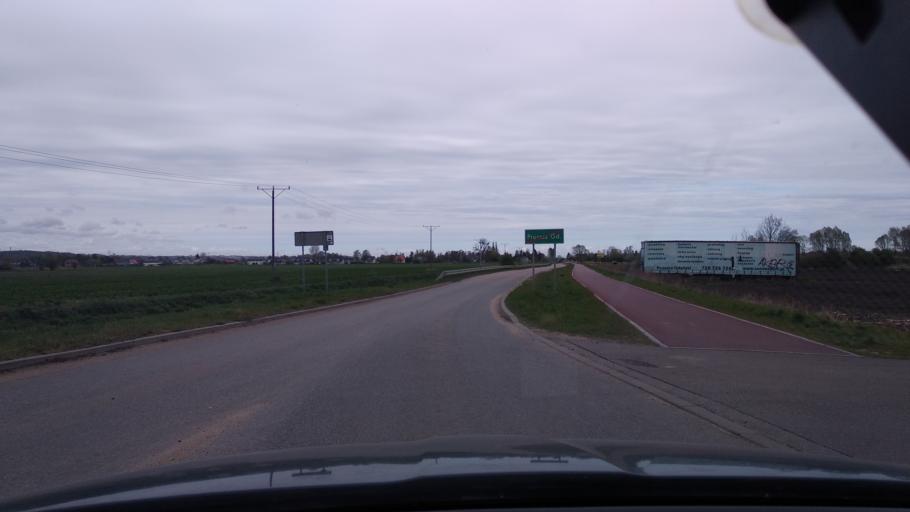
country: PL
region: Pomeranian Voivodeship
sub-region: Powiat gdanski
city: Pruszcz Gdanski
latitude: 54.2703
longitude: 18.6599
